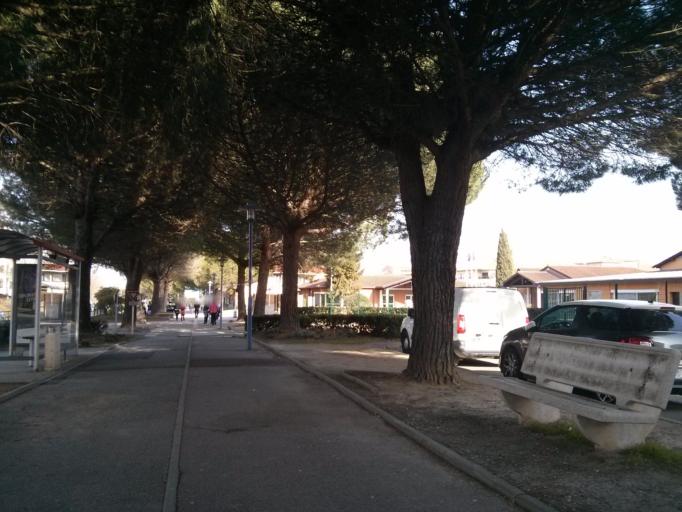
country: FR
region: Midi-Pyrenees
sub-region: Departement de la Haute-Garonne
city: Castanet-Tolosan
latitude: 43.5181
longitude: 1.5046
